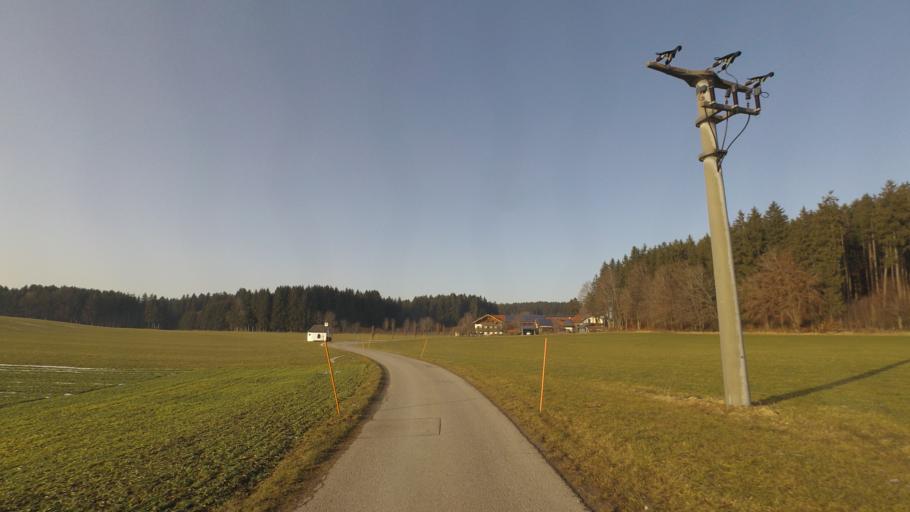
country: DE
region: Bavaria
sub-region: Upper Bavaria
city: Nussdorf
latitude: 47.9133
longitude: 12.5889
